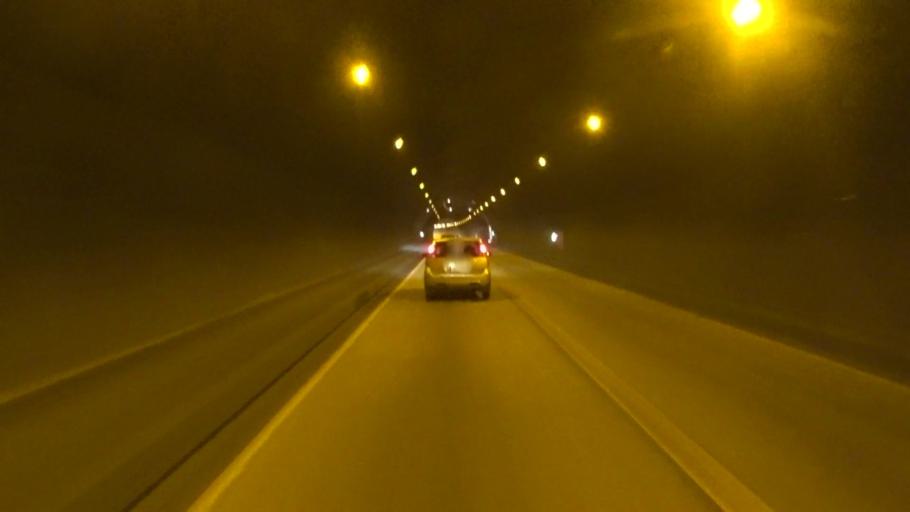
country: JP
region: Kyoto
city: Miyazu
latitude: 35.5492
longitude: 135.1759
